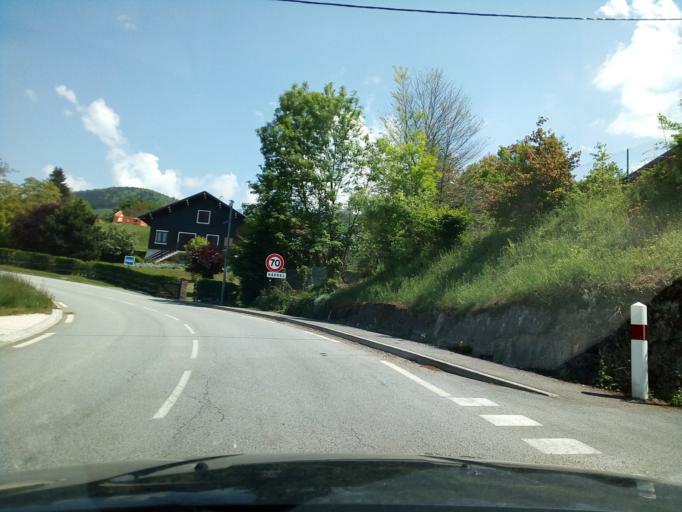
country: FR
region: Rhone-Alpes
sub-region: Departement de l'Isere
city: Revel
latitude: 45.1503
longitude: 5.8443
